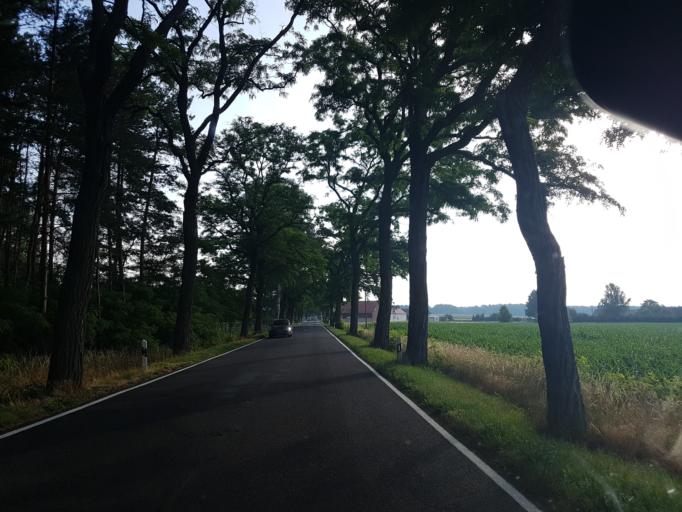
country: DE
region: Brandenburg
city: Schlieben
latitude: 51.7573
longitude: 13.3495
